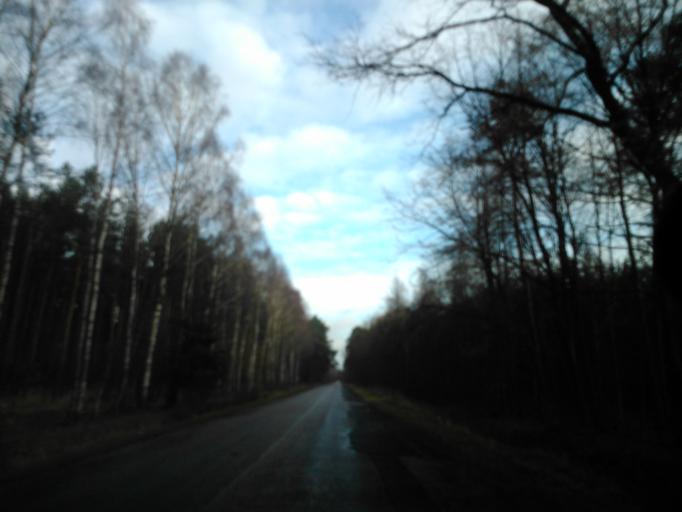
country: PL
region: Kujawsko-Pomorskie
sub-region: Powiat golubsko-dobrzynski
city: Golub-Dobrzyn
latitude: 53.1563
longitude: 19.1177
